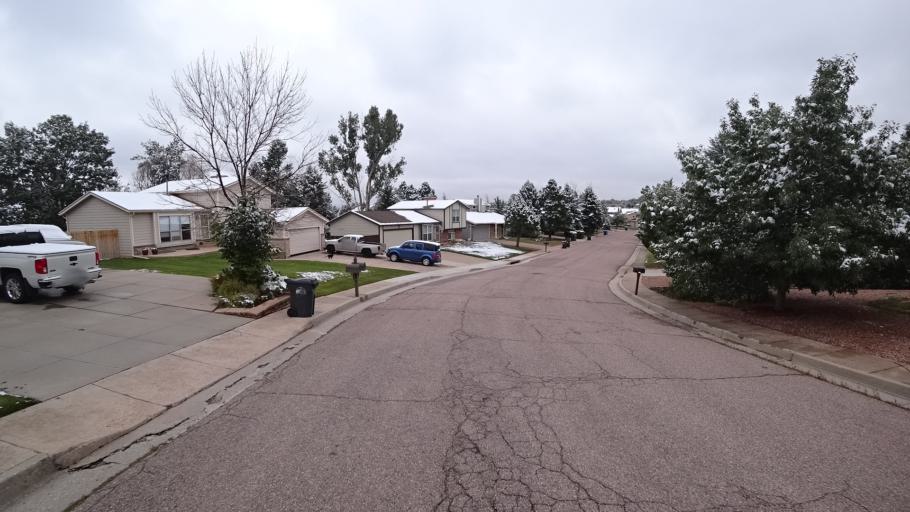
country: US
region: Colorado
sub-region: El Paso County
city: Colorado Springs
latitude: 38.9278
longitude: -104.7796
